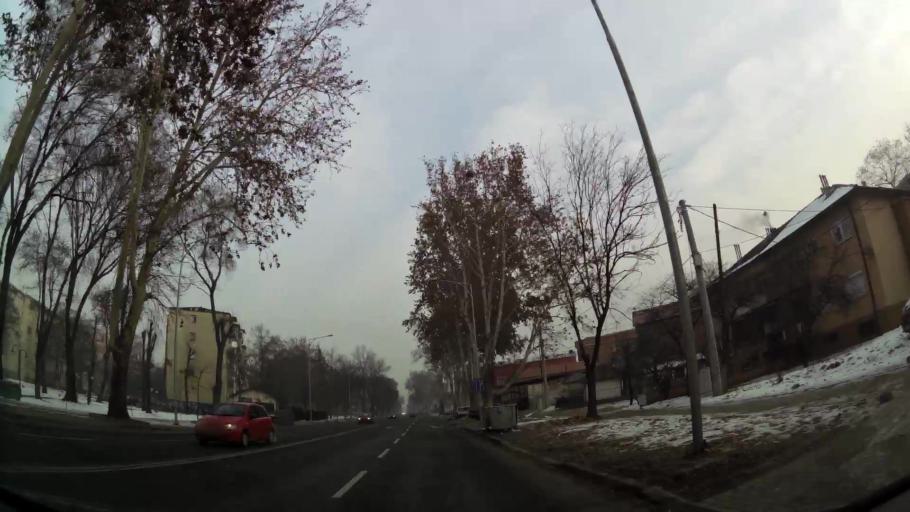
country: MK
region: Cair
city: Cair
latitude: 42.0155
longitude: 21.4466
